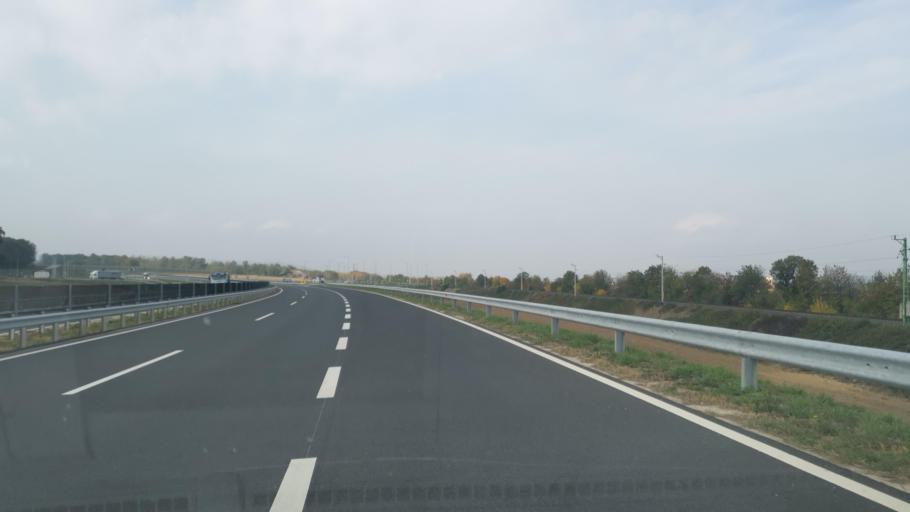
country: AT
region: Burgenland
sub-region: Politischer Bezirk Oberpullendorf
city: Deutschkreutz
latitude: 47.6260
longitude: 16.6517
